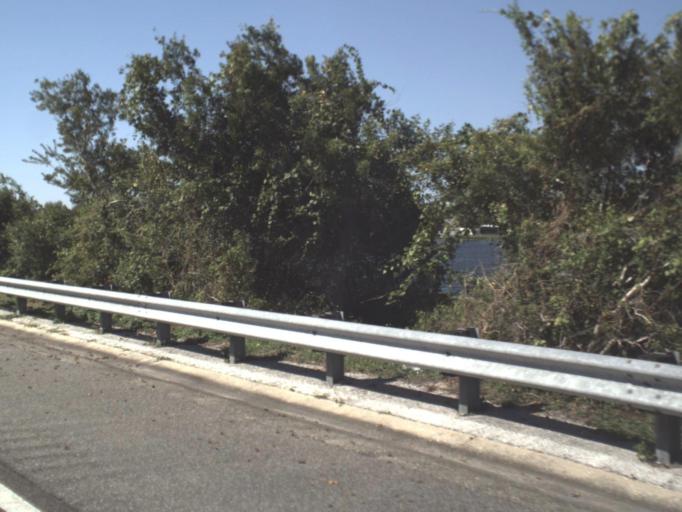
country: US
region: Florida
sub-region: Hillsborough County
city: Cheval
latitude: 28.1337
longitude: -82.5181
